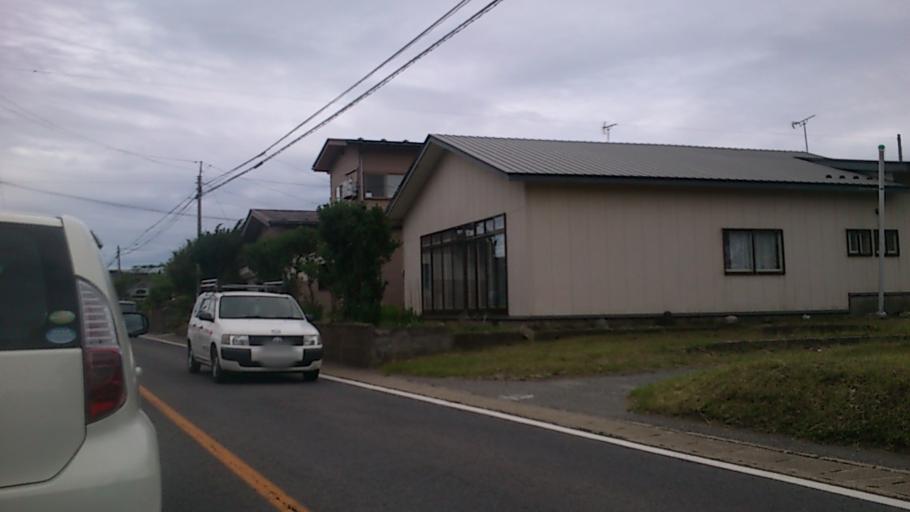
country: JP
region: Akita
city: Akita Shi
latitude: 39.6280
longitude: 140.0651
